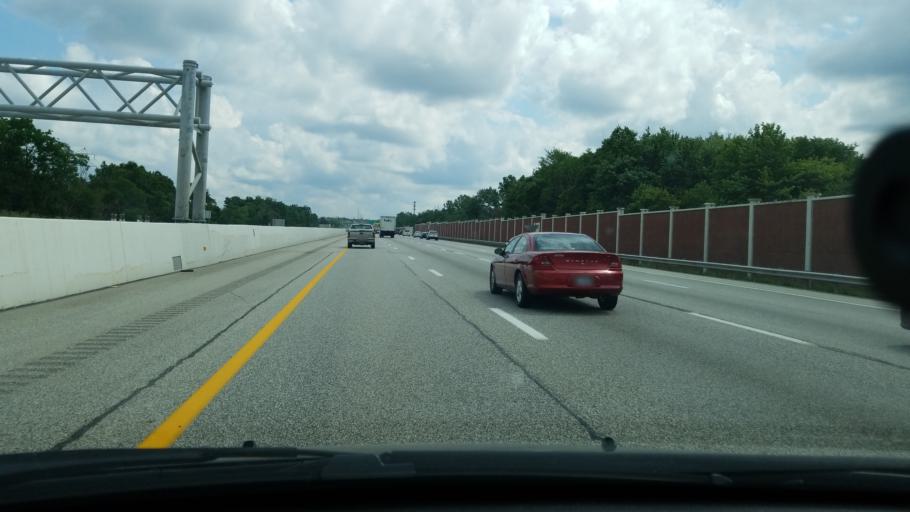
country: US
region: Ohio
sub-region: Cuyahoga County
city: Independence
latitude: 41.3717
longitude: -81.6521
